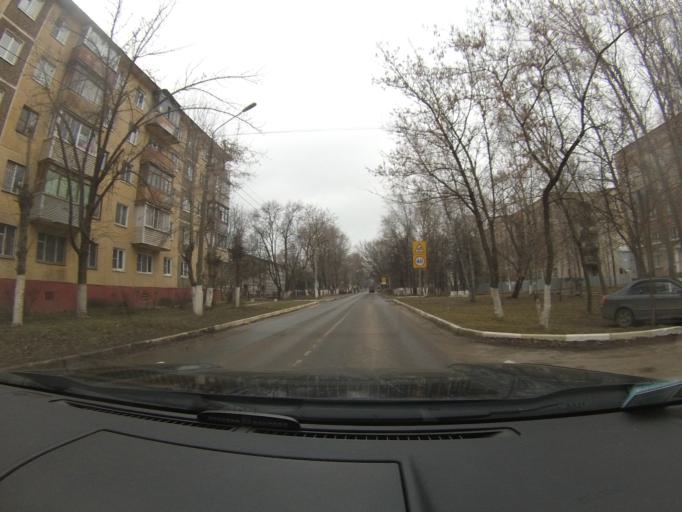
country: RU
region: Moskovskaya
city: Peski
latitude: 55.2703
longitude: 38.7476
